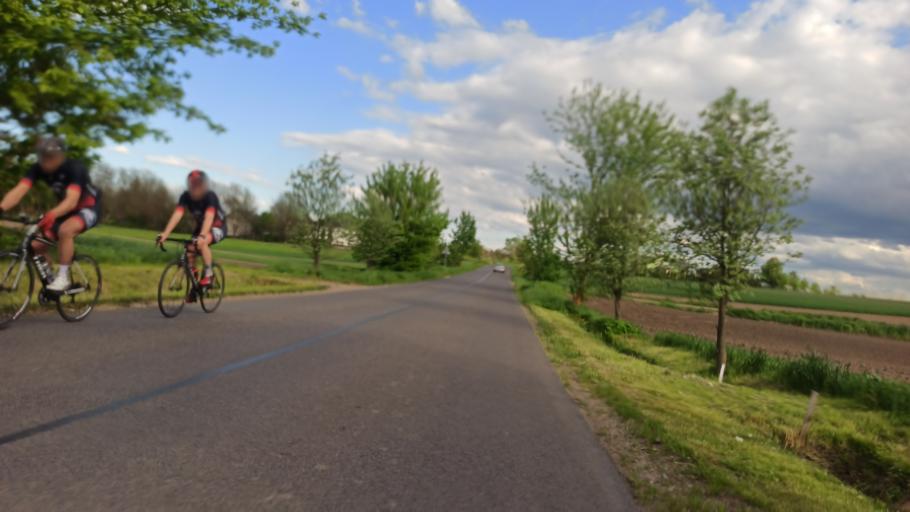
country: PL
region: Subcarpathian Voivodeship
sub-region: Powiat jaroslawski
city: Sosnica
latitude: 49.9219
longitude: 22.8535
